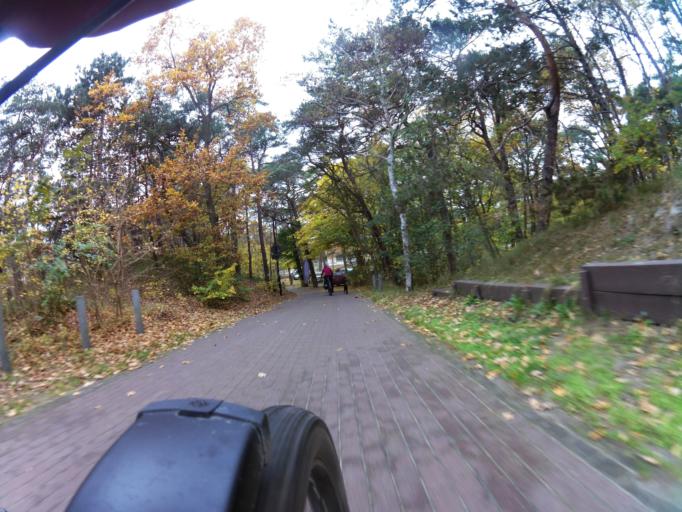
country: PL
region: Pomeranian Voivodeship
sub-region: Powiat pucki
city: Jastarnia
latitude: 54.6992
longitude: 18.6841
